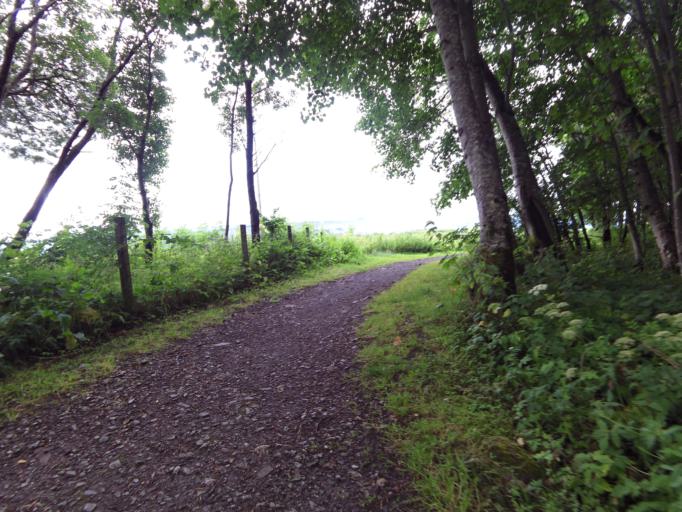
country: GB
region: Scotland
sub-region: Highland
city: Fort William
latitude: 56.8248
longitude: -5.1004
